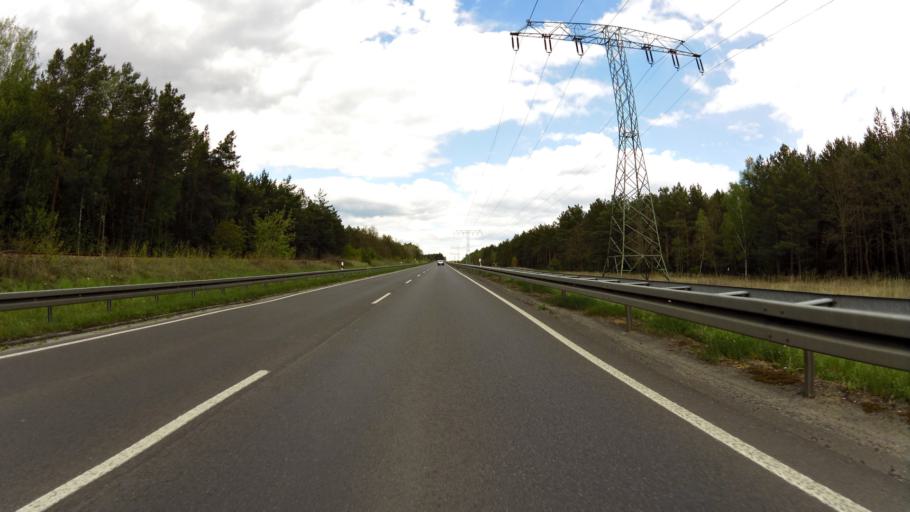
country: DE
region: Brandenburg
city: Langewahl
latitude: 52.3570
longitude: 14.1038
